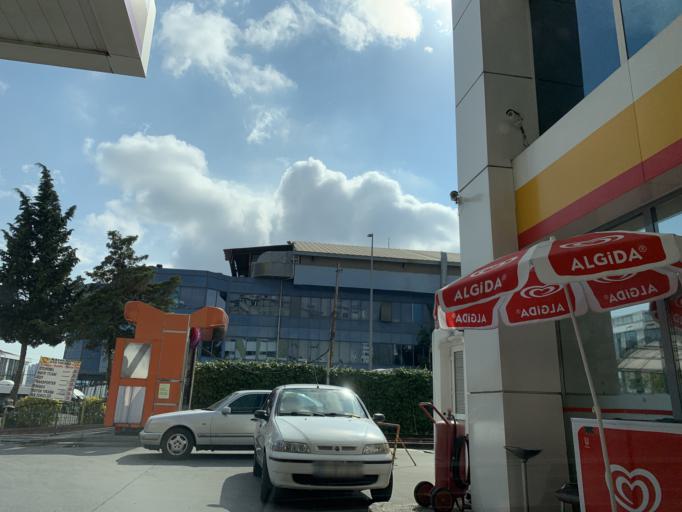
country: TR
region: Istanbul
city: Esenyurt
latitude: 41.0320
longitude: 28.6743
